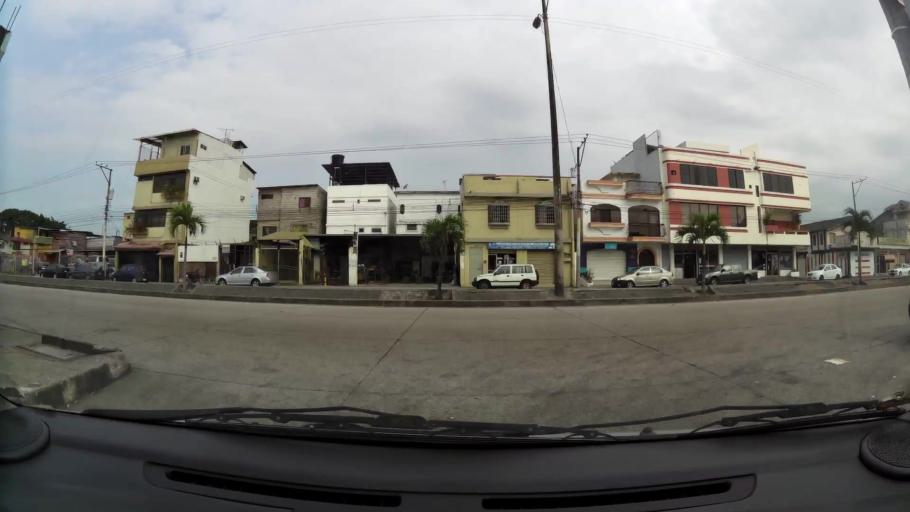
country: EC
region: Guayas
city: Eloy Alfaro
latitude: -2.1402
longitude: -79.8863
